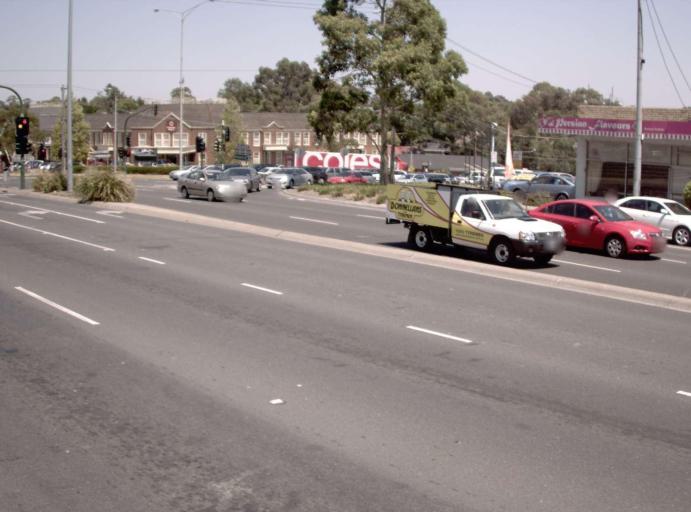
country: AU
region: Victoria
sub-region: Whitehorse
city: Forest Hill
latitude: -37.8341
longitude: 145.1730
